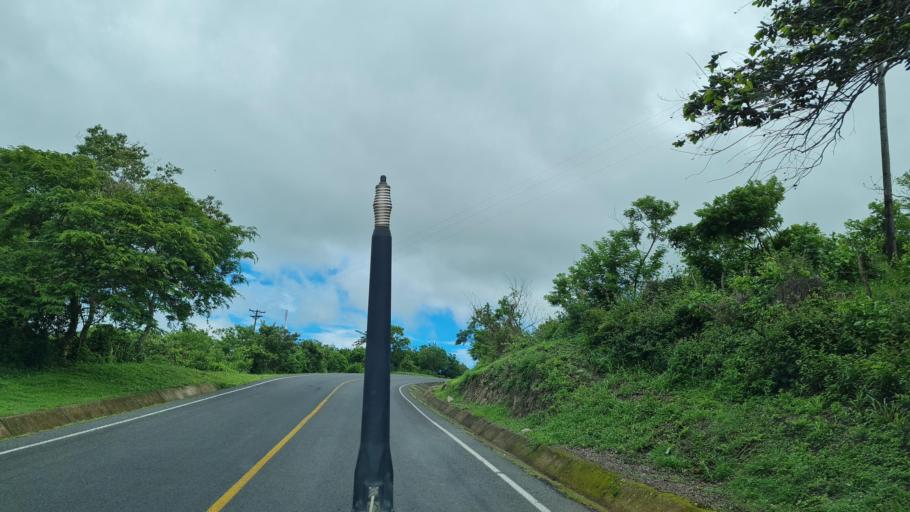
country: NI
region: Matagalpa
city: Terrabona
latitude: 12.5846
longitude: -85.9808
